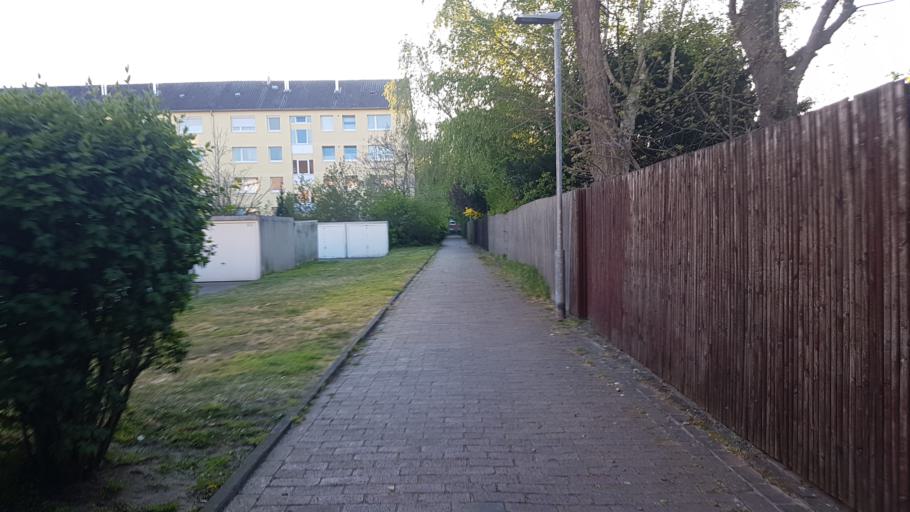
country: DE
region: Lower Saxony
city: Langenhagen
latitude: 52.4121
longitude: 9.7456
